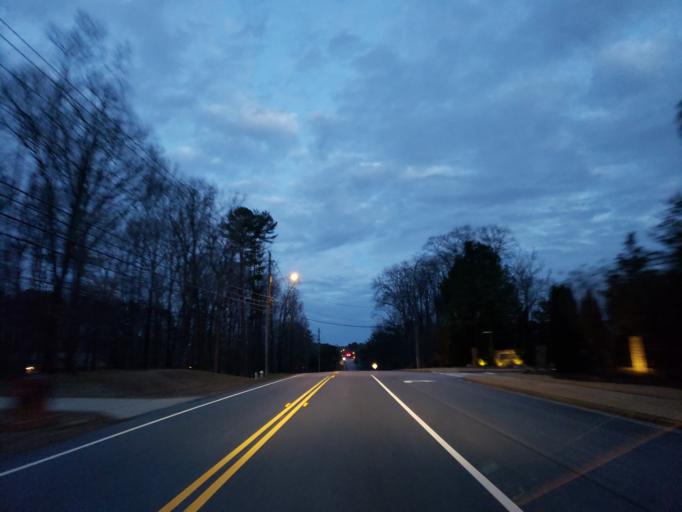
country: US
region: Georgia
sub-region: Cobb County
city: Kennesaw
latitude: 33.9993
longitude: -84.6659
